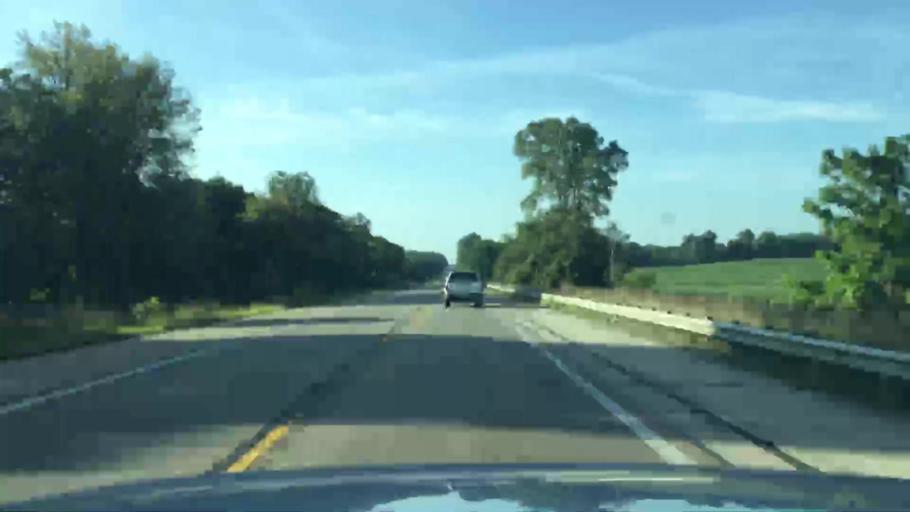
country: US
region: Michigan
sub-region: Jackson County
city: Vandercook Lake
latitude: 42.1010
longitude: -84.3639
